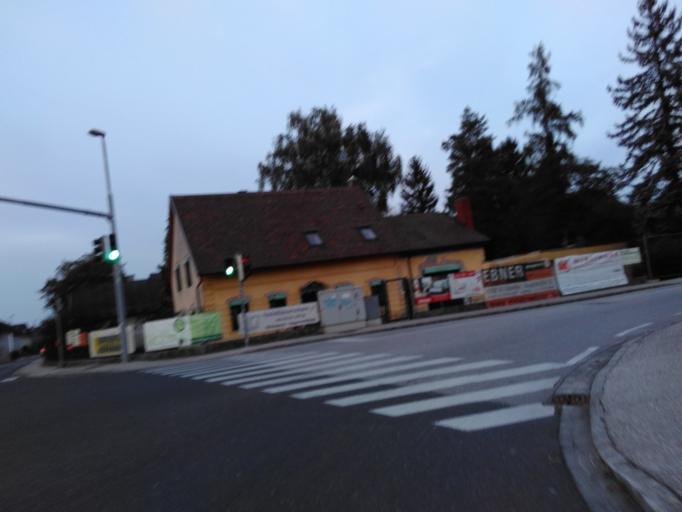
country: AT
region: Lower Austria
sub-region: Politischer Bezirk Amstetten
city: Sankt Valentin
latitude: 48.1716
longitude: 14.5125
